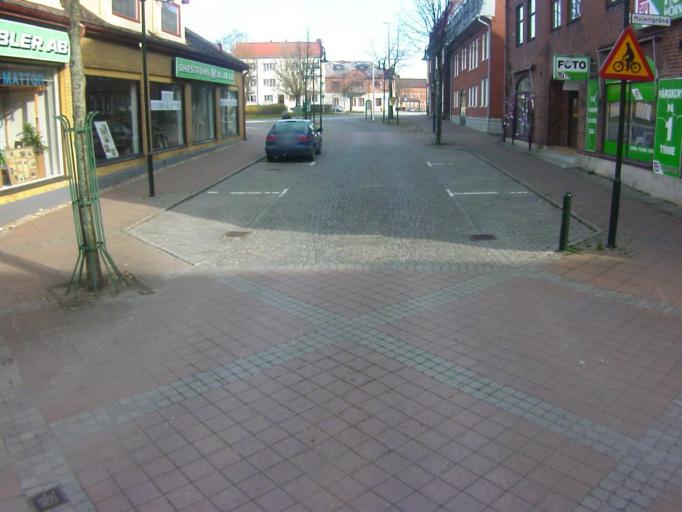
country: SE
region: Skane
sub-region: Kavlinge Kommun
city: Kaevlinge
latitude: 55.7922
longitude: 13.1103
